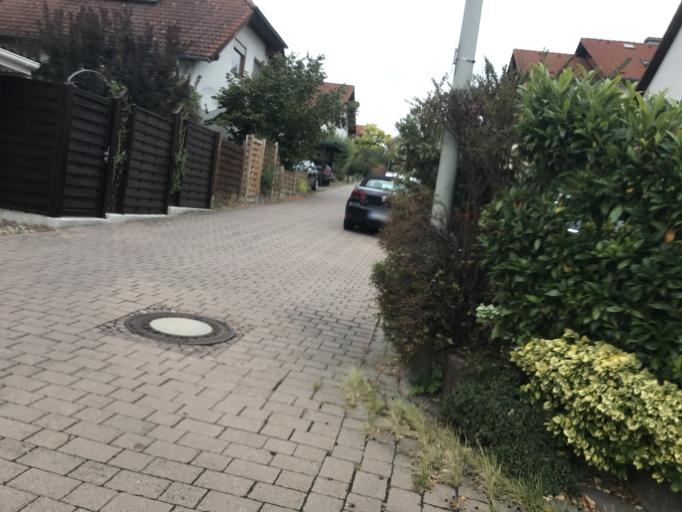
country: DE
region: Rheinland-Pfalz
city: Jugenheim
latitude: 49.8916
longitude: 8.0815
